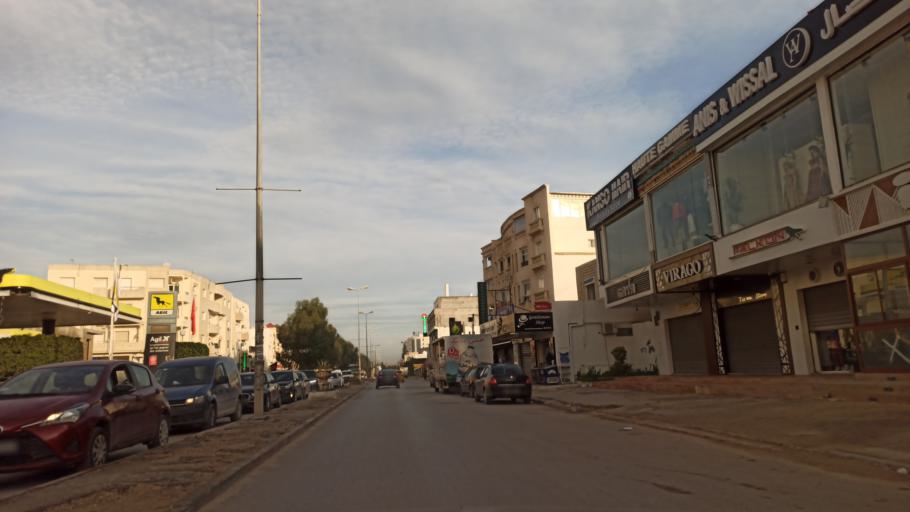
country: TN
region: Tunis
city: La Goulette
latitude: 36.8542
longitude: 10.2575
